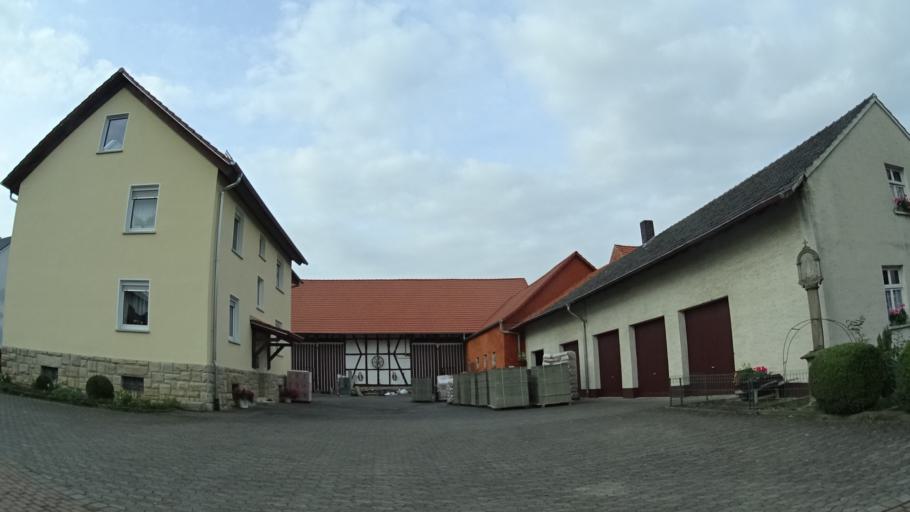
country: DE
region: Hesse
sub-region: Regierungsbezirk Kassel
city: Hofbieber
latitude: 50.5790
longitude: 9.8049
